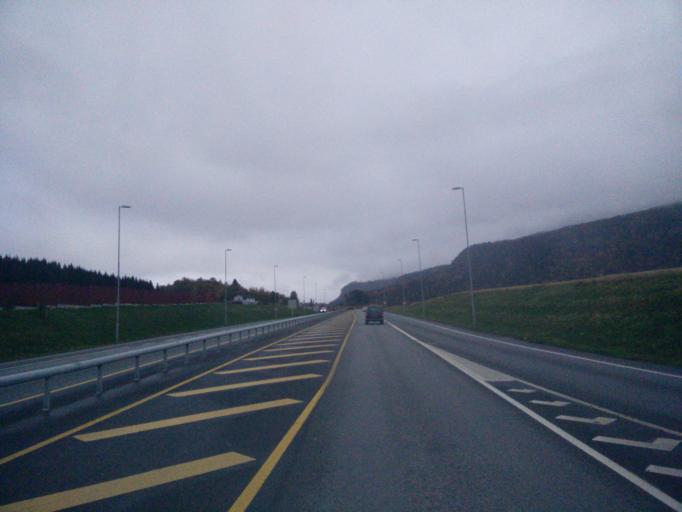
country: NO
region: Nord-Trondelag
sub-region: Stjordal
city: Stjordal
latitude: 63.4911
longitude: 10.8848
